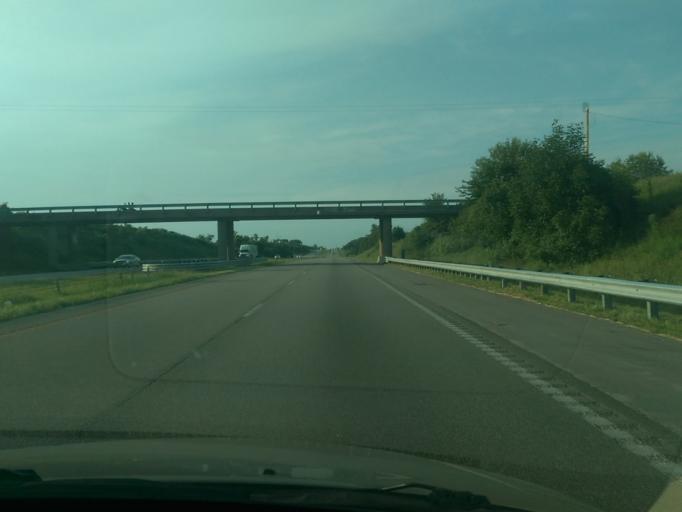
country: US
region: Missouri
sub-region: Platte County
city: Platte City
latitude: 39.4184
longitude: -94.7896
